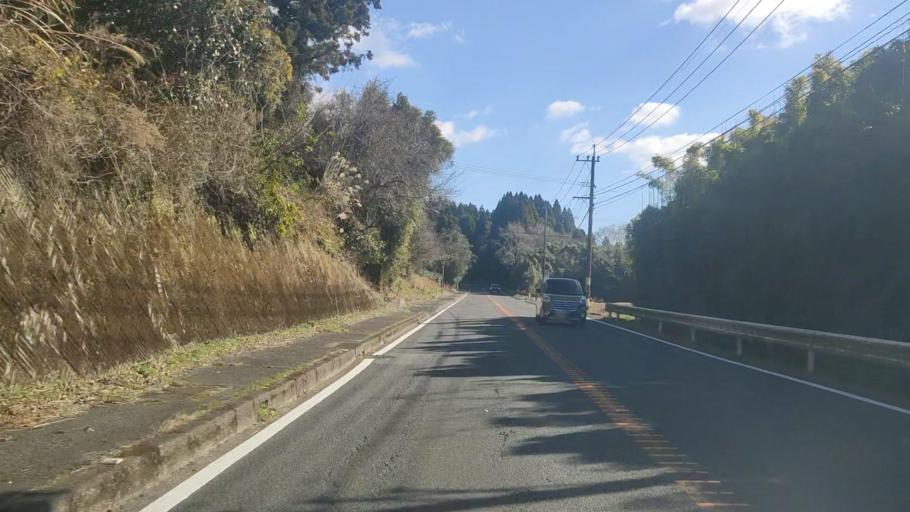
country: JP
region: Kagoshima
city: Sueyoshicho-ninokata
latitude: 31.6629
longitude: 130.9006
